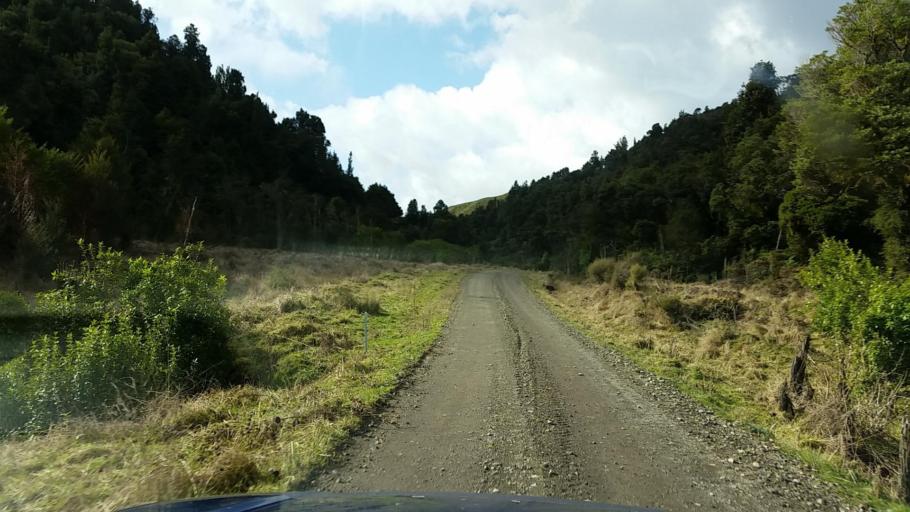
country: NZ
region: Taranaki
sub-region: South Taranaki District
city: Eltham
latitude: -39.2586
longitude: 174.7924
